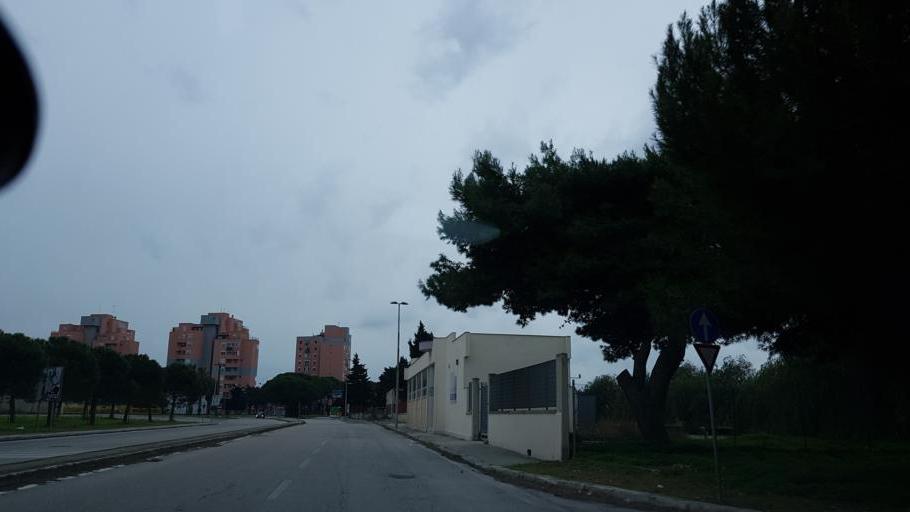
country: IT
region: Apulia
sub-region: Provincia di Brindisi
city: Brindisi
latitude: 40.6349
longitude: 17.9539
